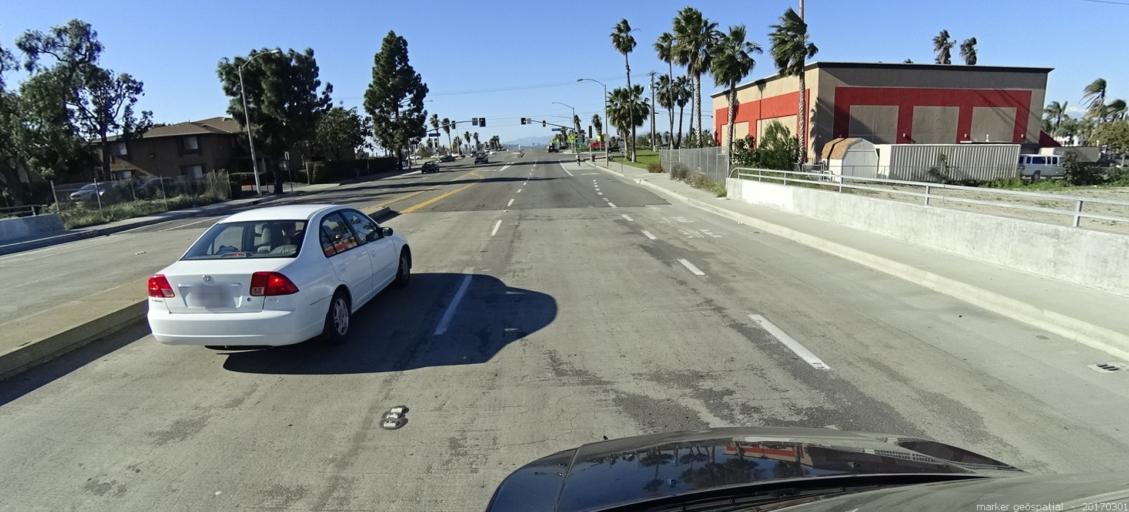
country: US
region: California
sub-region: Orange County
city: Placentia
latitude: 33.8454
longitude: -117.8539
